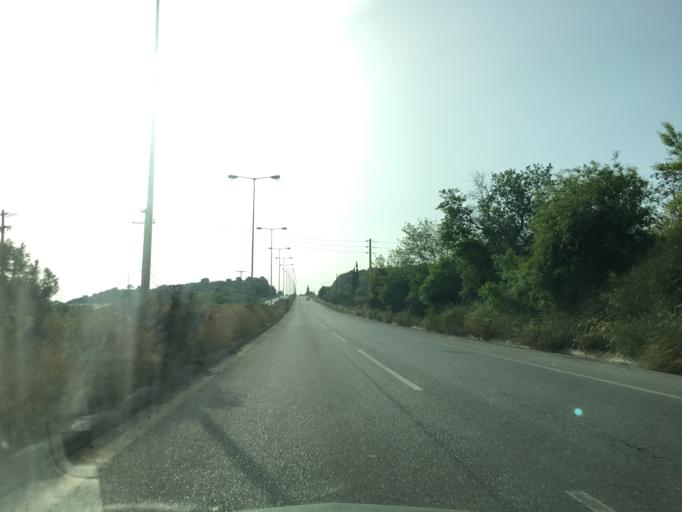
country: GR
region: Thessaly
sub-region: Nomos Magnisias
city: Nea Ionia
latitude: 39.3760
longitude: 22.8933
